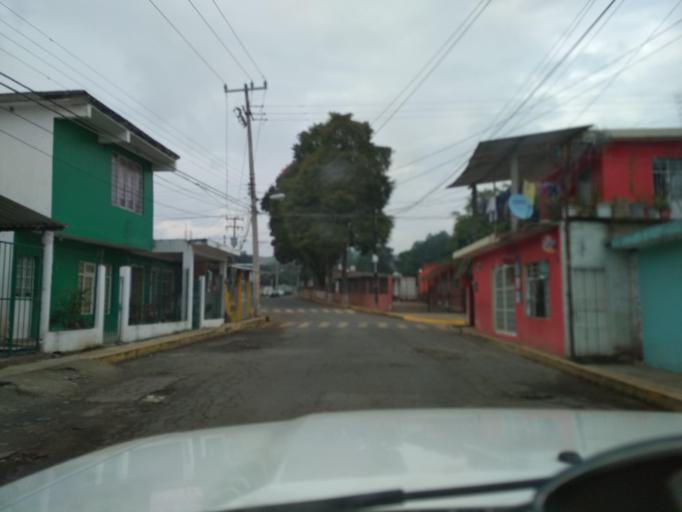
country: MX
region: Veracruz
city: El Castillo
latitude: 19.5647
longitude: -96.8646
